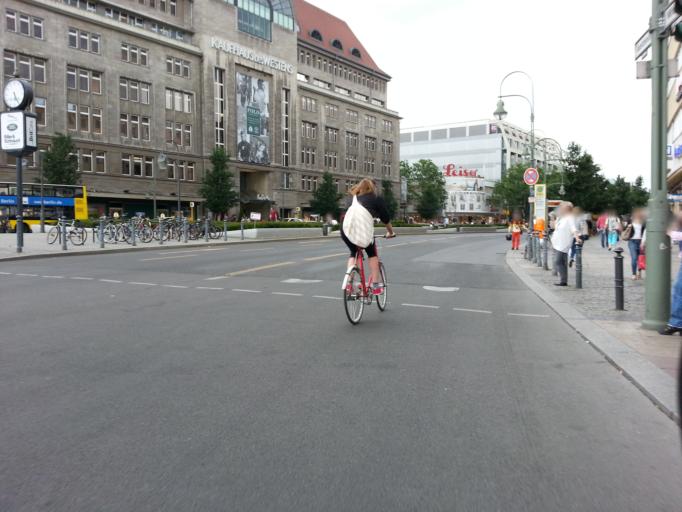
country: DE
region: Berlin
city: Hansaviertel
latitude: 52.5022
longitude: 13.3424
